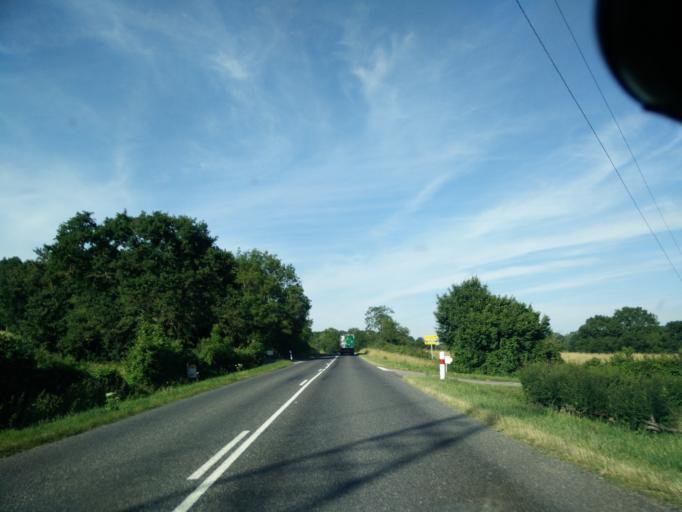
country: FR
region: Auvergne
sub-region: Departement de l'Allier
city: Souvigny
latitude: 46.5449
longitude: 3.2250
